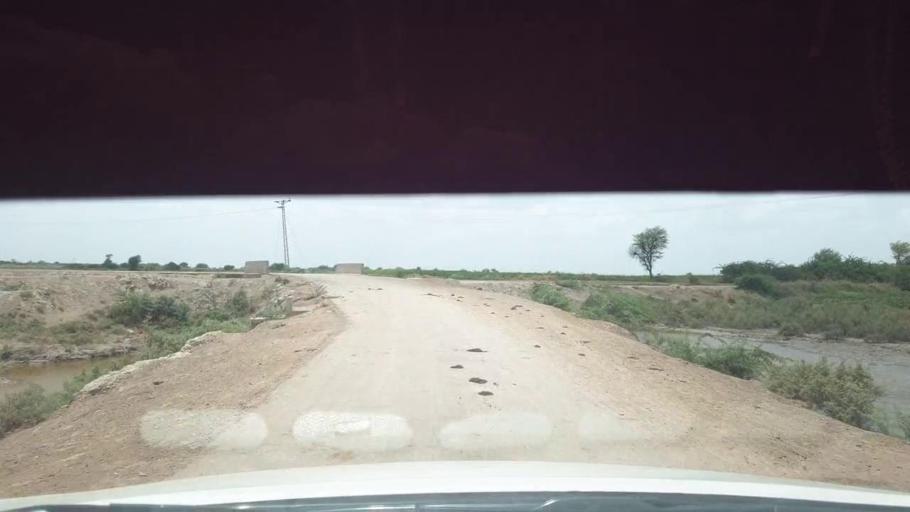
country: PK
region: Sindh
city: Kadhan
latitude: 24.5493
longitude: 69.1190
